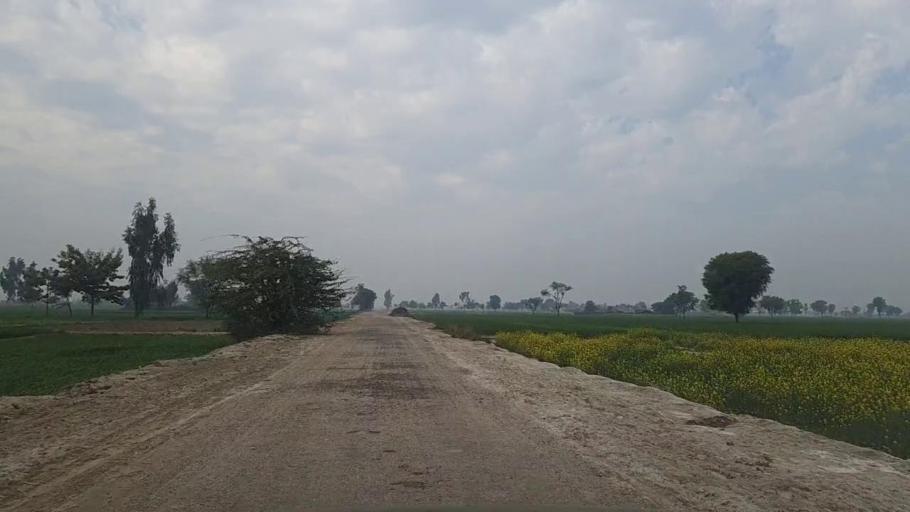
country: PK
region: Sindh
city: Nawabshah
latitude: 26.3560
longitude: 68.3978
